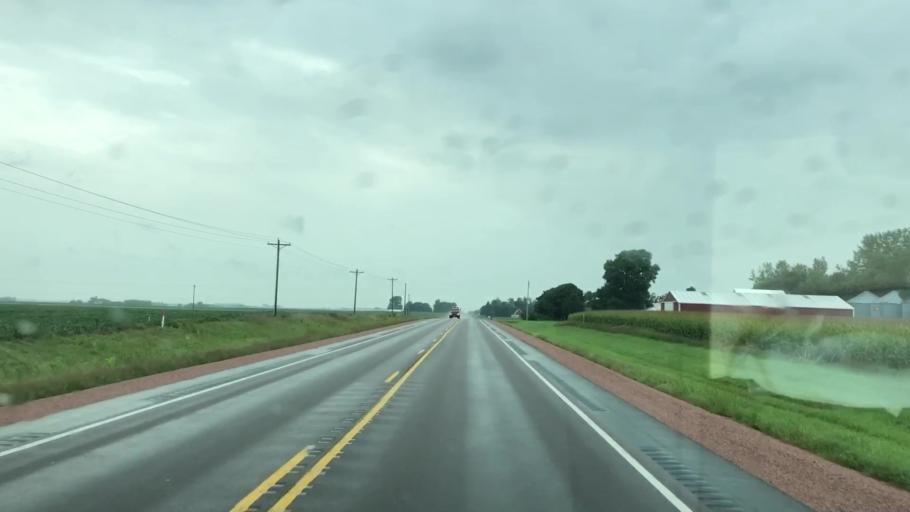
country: US
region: Iowa
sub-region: O'Brien County
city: Sanborn
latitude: 43.1862
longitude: -95.7345
